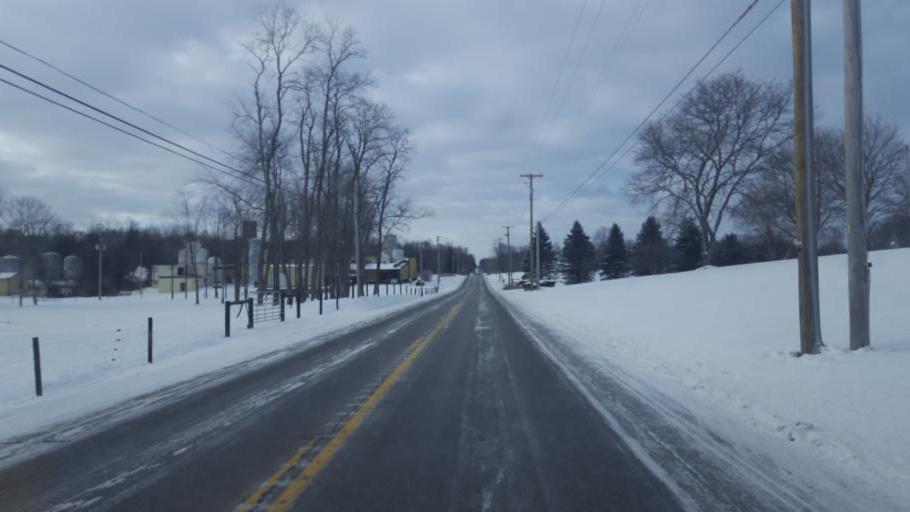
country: US
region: Pennsylvania
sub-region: Mercer County
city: Mercer
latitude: 41.3408
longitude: -80.2271
